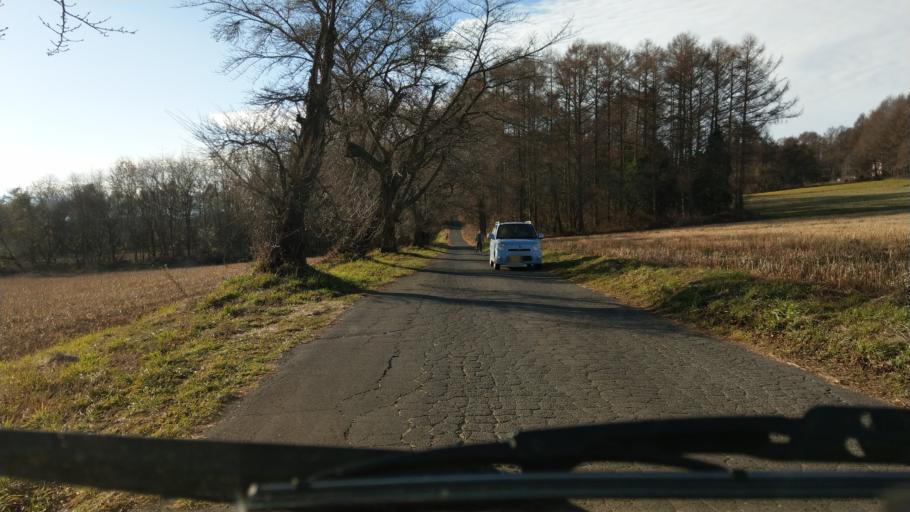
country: JP
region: Nagano
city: Komoro
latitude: 36.3436
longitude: 138.4610
